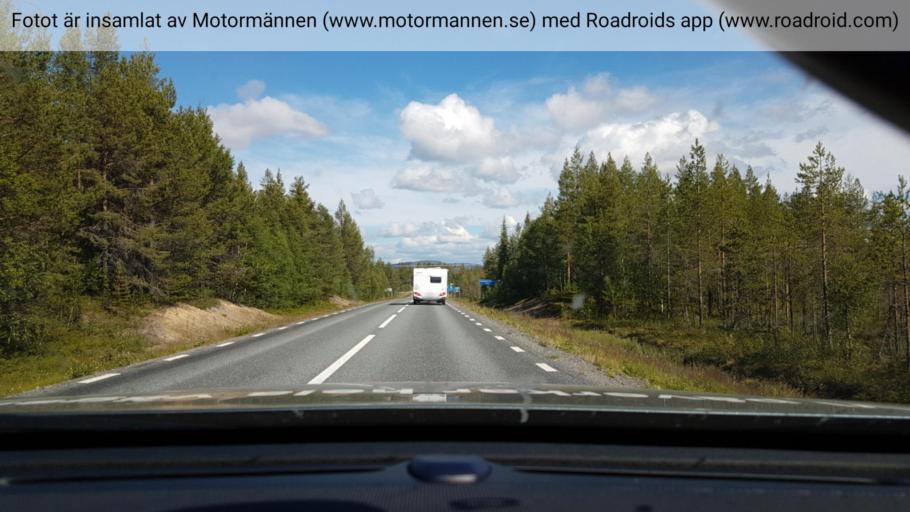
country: SE
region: Norrbotten
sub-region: Arjeplogs Kommun
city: Arjeplog
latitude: 65.5848
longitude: 18.1431
